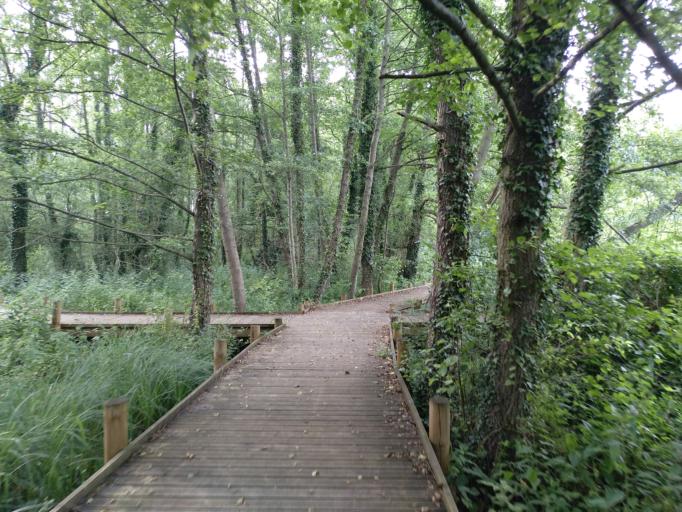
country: FR
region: Rhone-Alpes
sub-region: Departement du Rhone
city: Marennes
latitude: 45.6323
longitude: 4.9260
